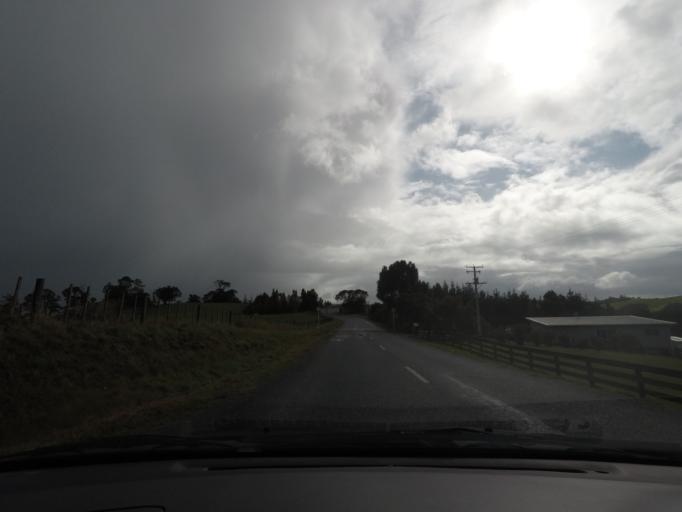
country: NZ
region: Auckland
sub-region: Auckland
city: Warkworth
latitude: -36.4629
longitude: 174.7343
